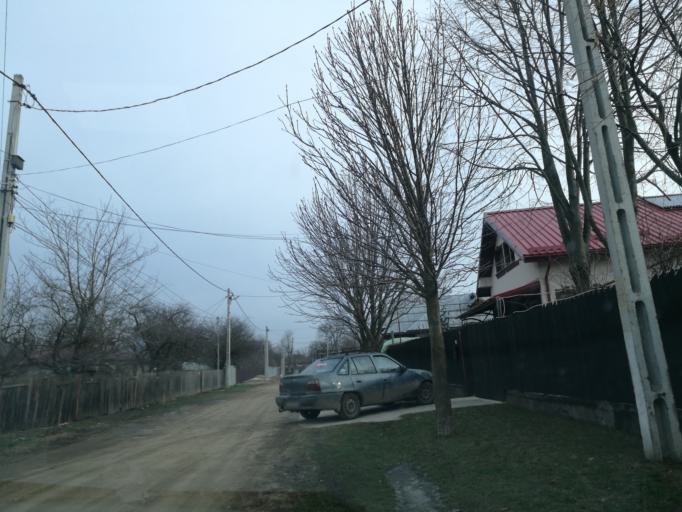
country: RO
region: Ialomita
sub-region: Comuna Fierbinti-Targ
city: Fierbintii de Jos
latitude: 44.6971
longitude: 26.4025
